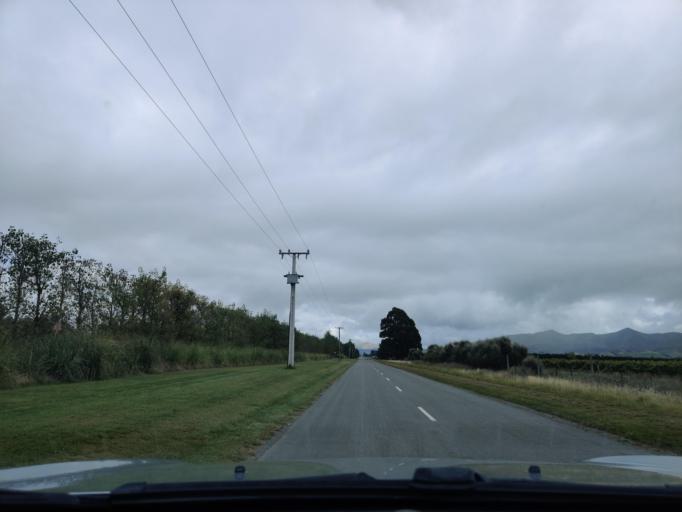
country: NZ
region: Canterbury
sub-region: Hurunui District
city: Amberley
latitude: -43.0766
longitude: 172.7125
